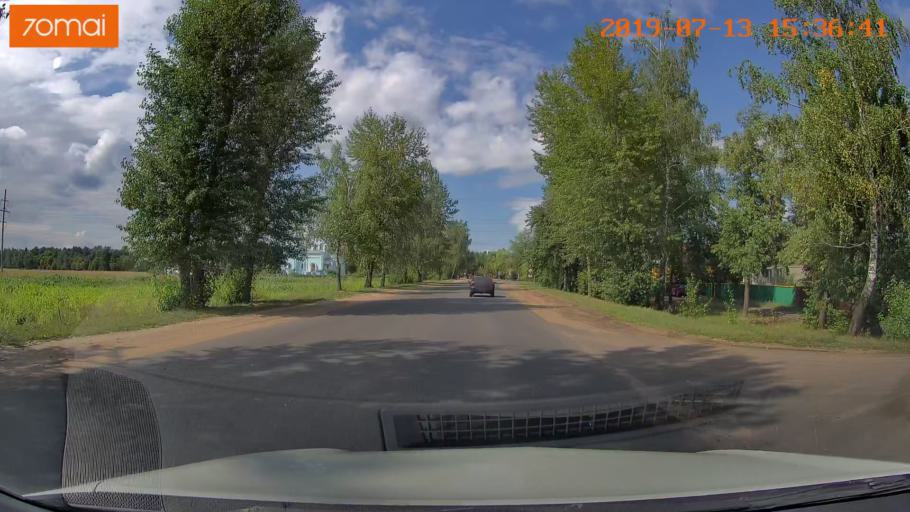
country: BY
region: Mogilev
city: Babruysk
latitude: 53.1337
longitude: 29.1666
